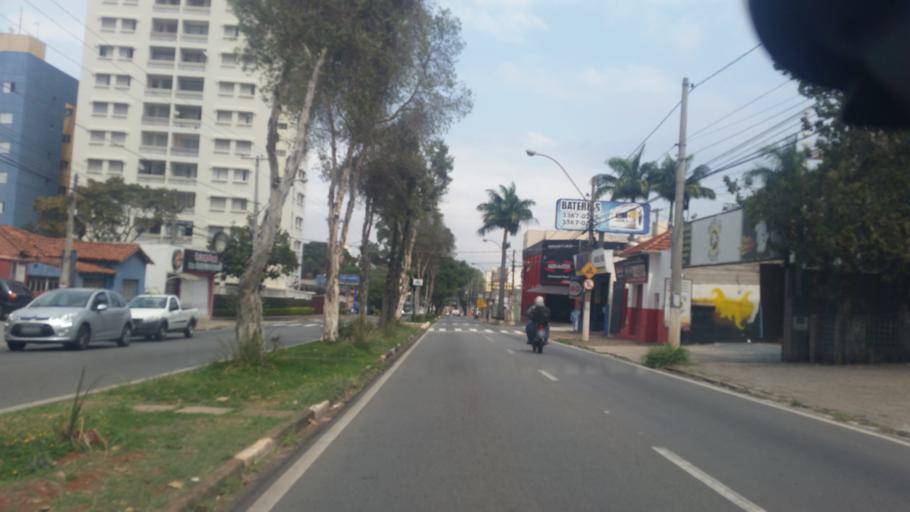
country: BR
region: Sao Paulo
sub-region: Campinas
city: Campinas
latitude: -22.8952
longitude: -47.0794
